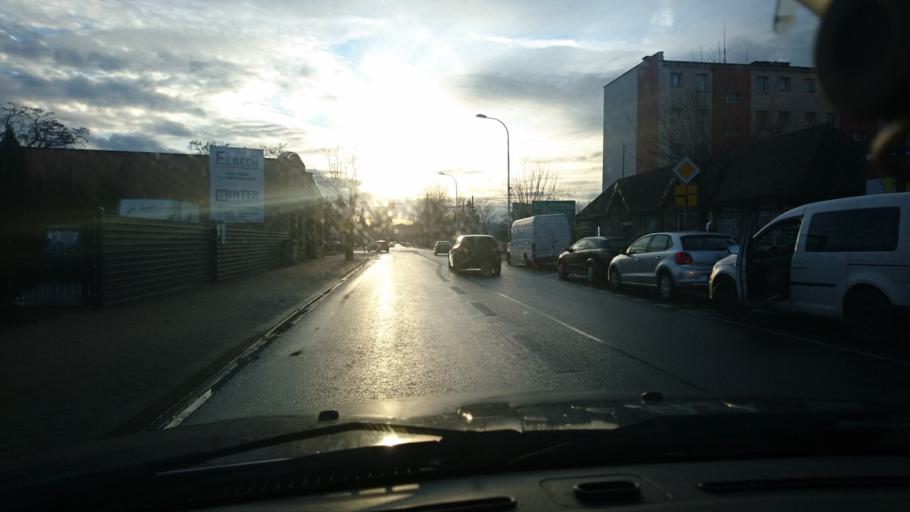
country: PL
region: Greater Poland Voivodeship
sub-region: Powiat kepinski
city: Kepno
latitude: 51.2839
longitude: 17.9914
